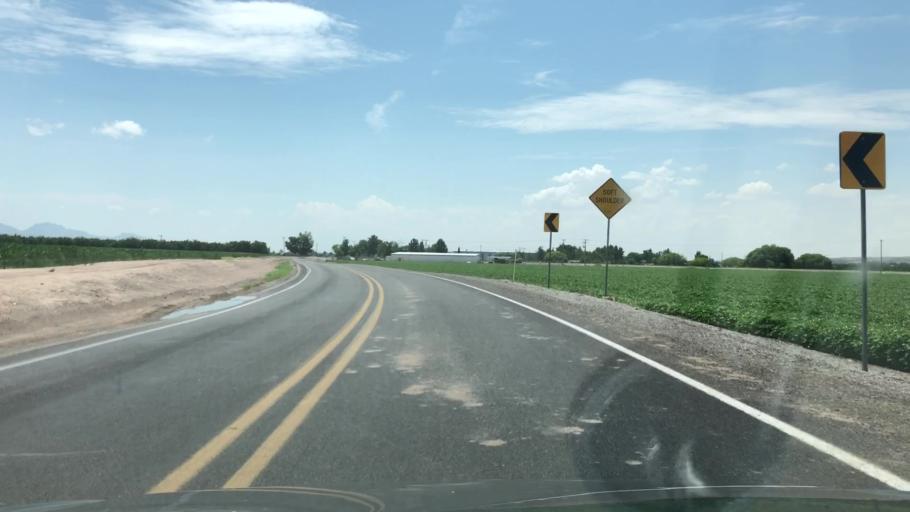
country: US
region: New Mexico
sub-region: Dona Ana County
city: Vado
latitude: 32.0653
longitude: -106.6790
